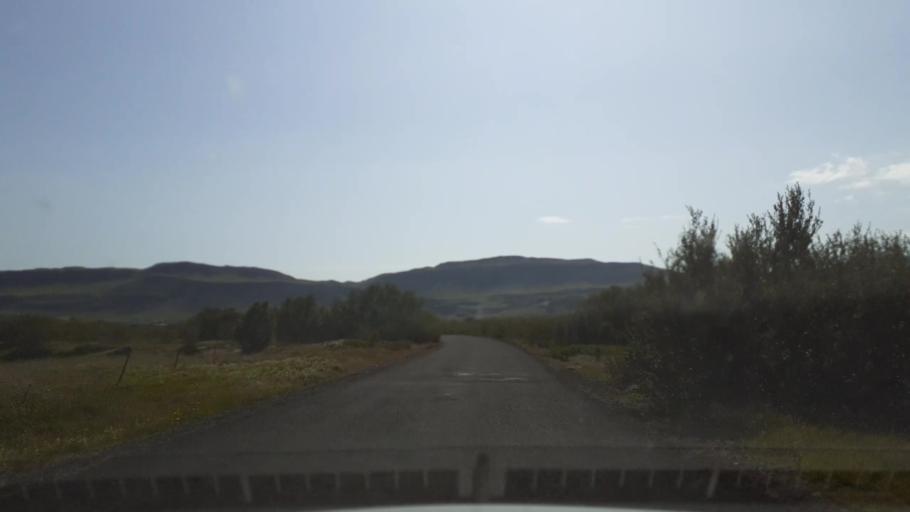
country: IS
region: West
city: Borgarnes
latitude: 64.7566
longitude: -21.5519
